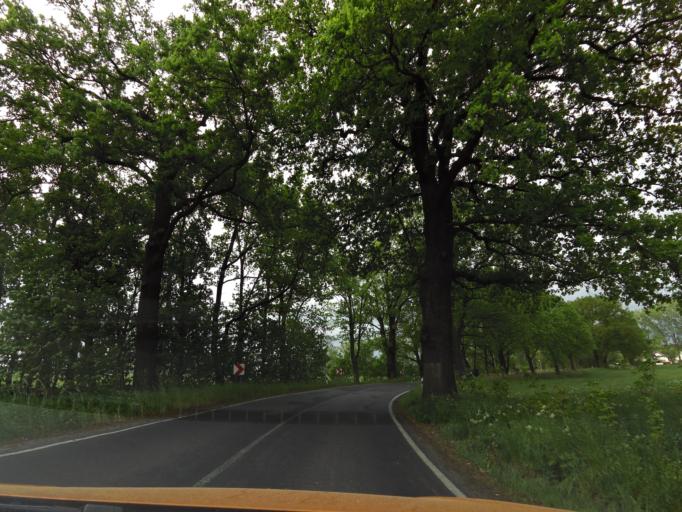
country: DE
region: Berlin
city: Wannsee
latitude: 52.3235
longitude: 13.1339
